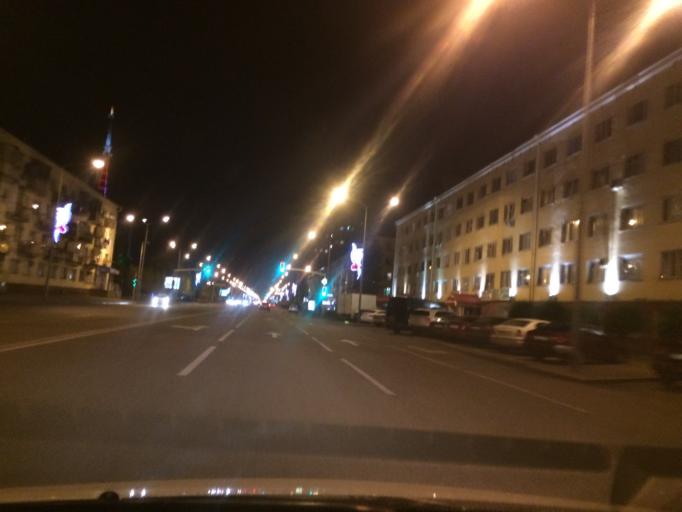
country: KZ
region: Astana Qalasy
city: Astana
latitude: 51.1889
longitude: 71.4073
